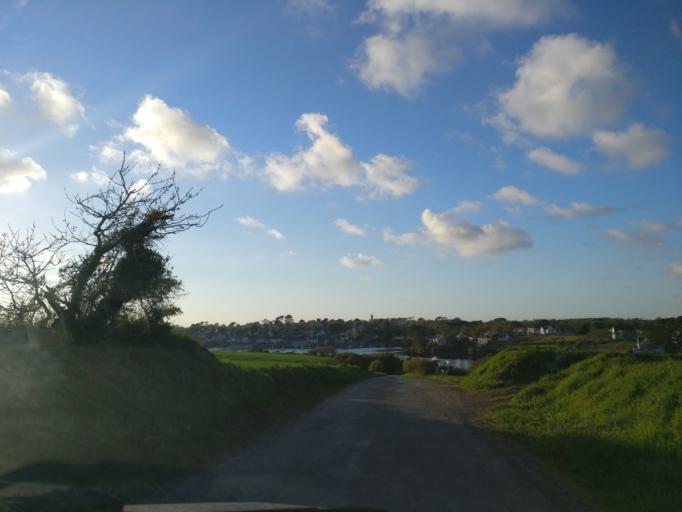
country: FR
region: Brittany
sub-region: Departement du Finistere
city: Lampaul-Plouarzel
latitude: 48.4687
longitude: -4.7461
